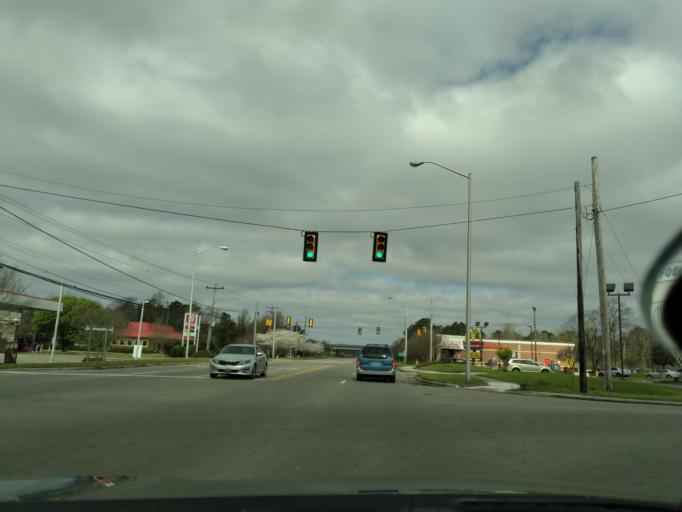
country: US
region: North Carolina
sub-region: Chowan County
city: Edenton
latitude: 36.0726
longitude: -76.6111
